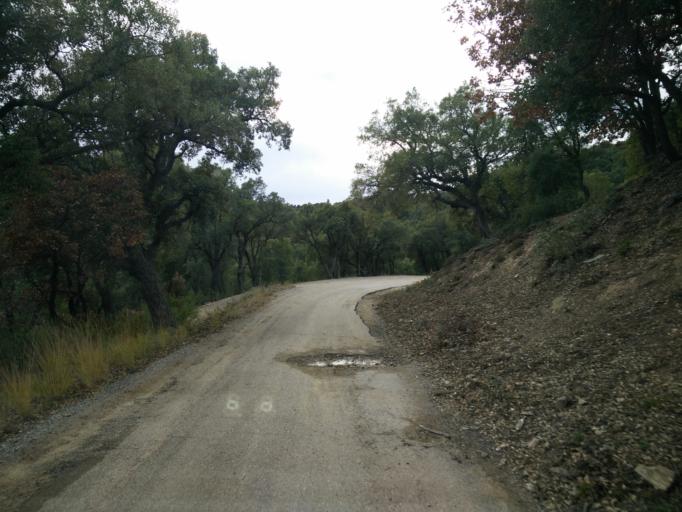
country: FR
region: Provence-Alpes-Cote d'Azur
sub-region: Departement du Var
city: Roquebrune-sur-Argens
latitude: 43.3968
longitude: 6.6107
